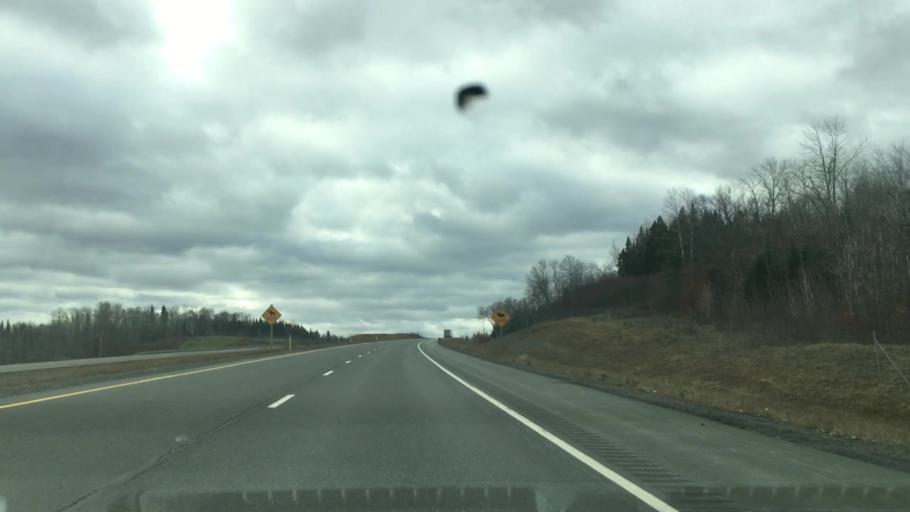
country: US
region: Maine
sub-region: Aroostook County
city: Fort Fairfield
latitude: 46.6630
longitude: -67.7321
